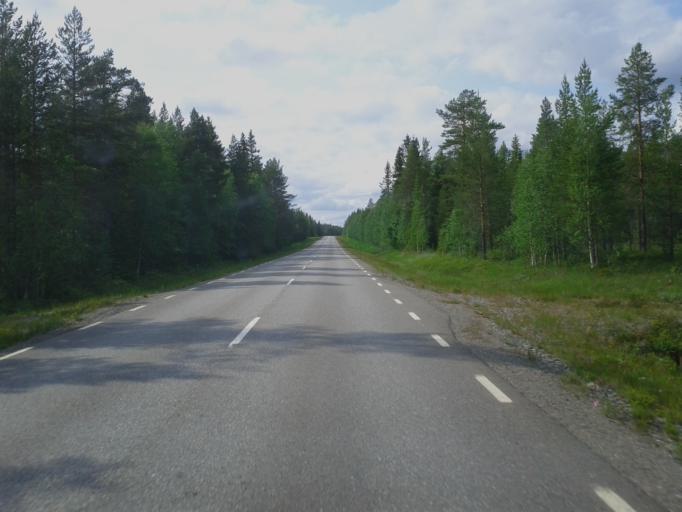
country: SE
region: Vaesterbotten
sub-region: Mala Kommun
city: Mala
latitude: 65.2308
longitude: 18.3486
